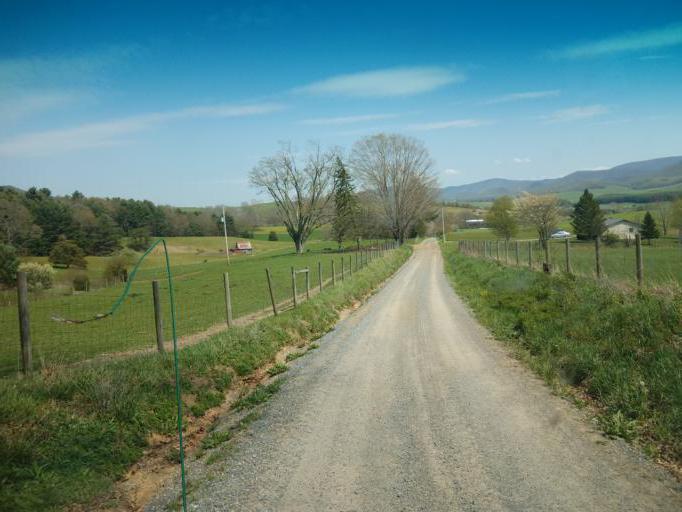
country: US
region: Virginia
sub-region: Smyth County
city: Marion
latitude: 36.7799
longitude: -81.4610
